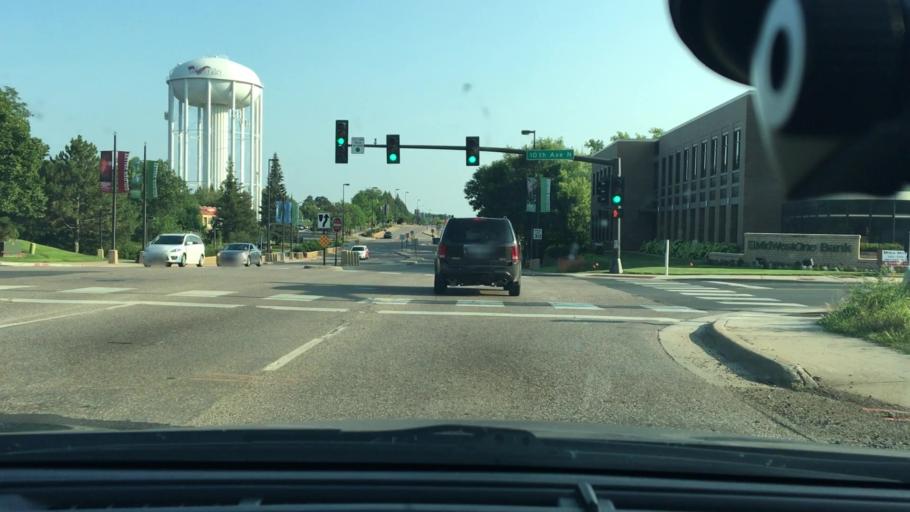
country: US
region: Minnesota
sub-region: Hennepin County
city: Golden Valley
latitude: 44.9894
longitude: -93.3805
